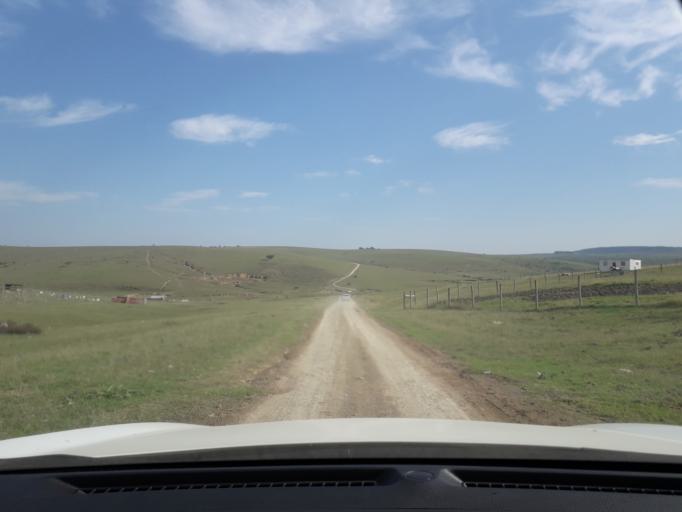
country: ZA
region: Eastern Cape
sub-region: Buffalo City Metropolitan Municipality
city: Bhisho
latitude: -33.0047
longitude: 27.3317
